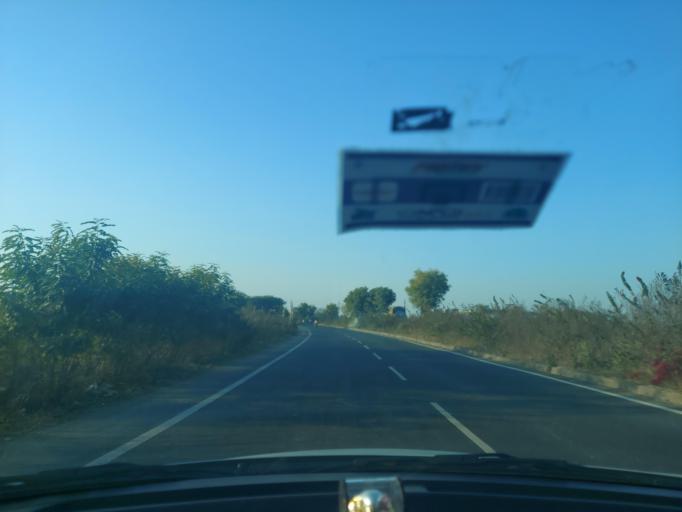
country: IN
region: Madhya Pradesh
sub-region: Indore
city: Sanwer
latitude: 23.0460
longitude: 75.8297
